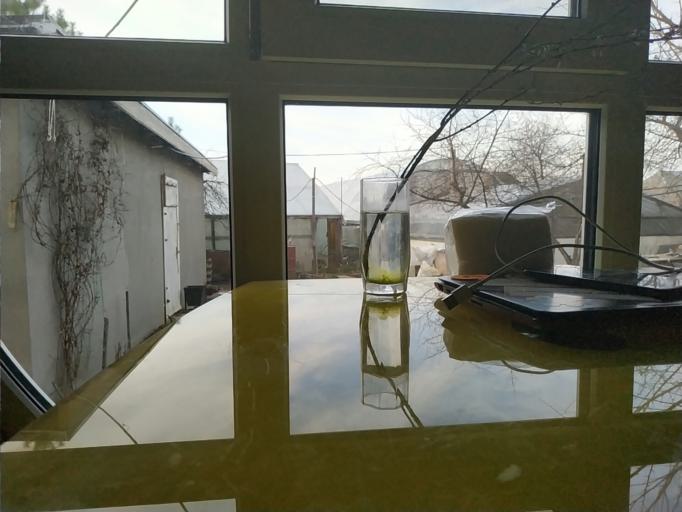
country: RU
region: Republic of Karelia
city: Suoyarvi
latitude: 61.9102
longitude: 32.2507
